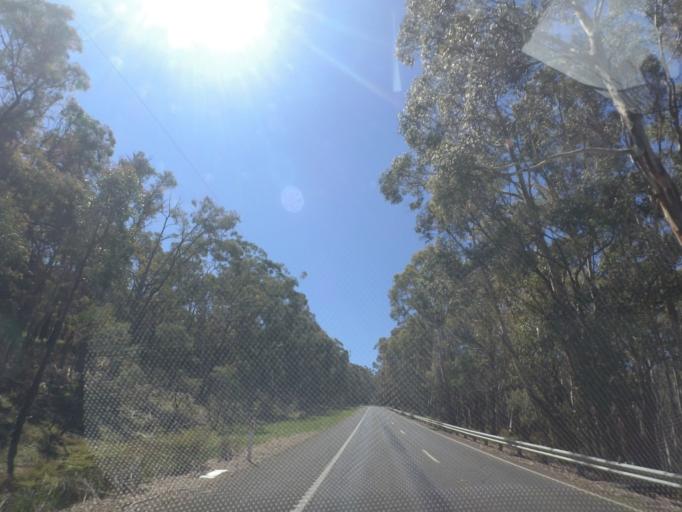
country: AU
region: Victoria
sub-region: Hume
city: Sunbury
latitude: -37.2310
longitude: 144.7405
